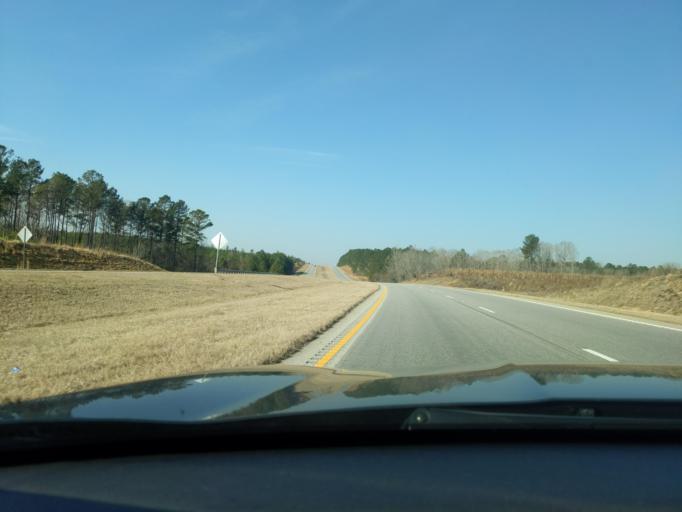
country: US
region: South Carolina
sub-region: Abbeville County
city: Calhoun Falls
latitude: 34.1134
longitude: -82.4801
